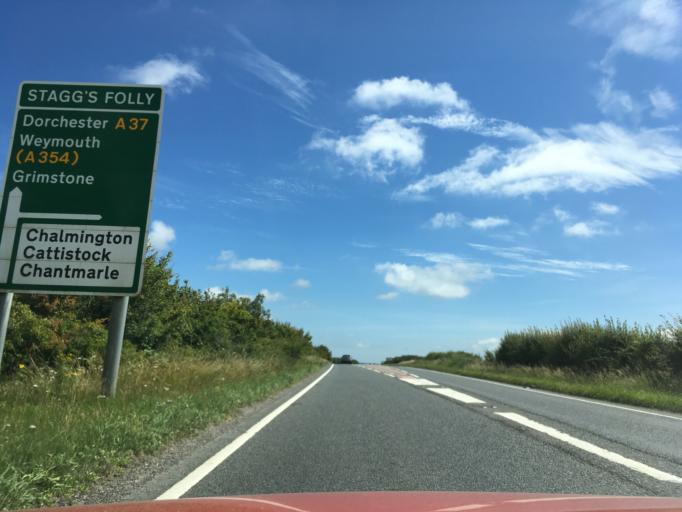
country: GB
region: England
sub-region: Dorset
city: Sherborne
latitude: 50.8049
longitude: -2.5517
